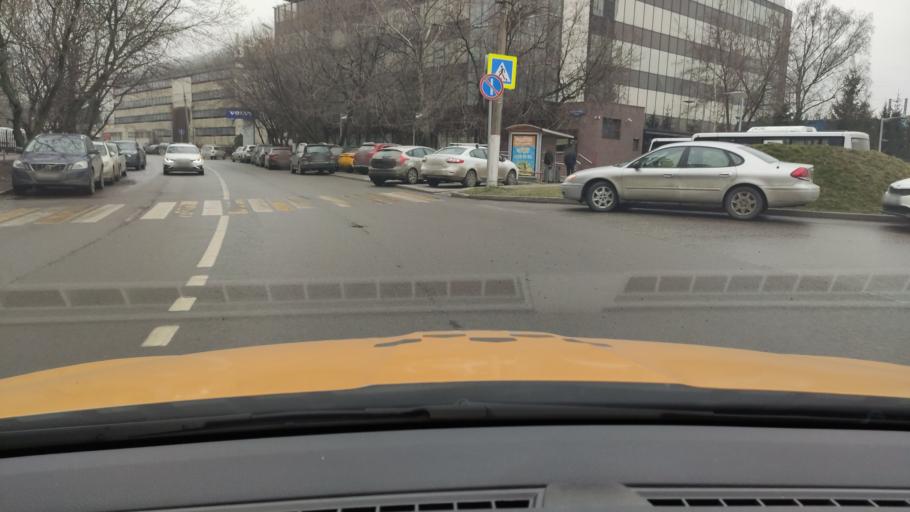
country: RU
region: Moscow
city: Khimki
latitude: 55.8802
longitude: 37.4316
